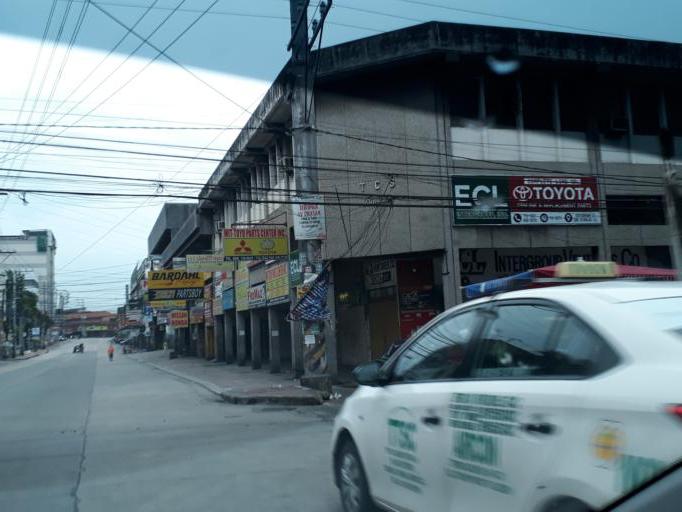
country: PH
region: Calabarzon
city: Del Monte
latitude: 14.6191
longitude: 121.0098
